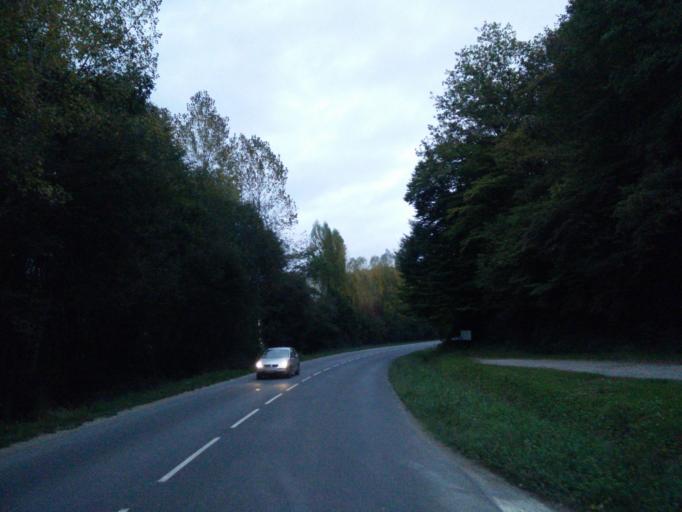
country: FR
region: Aquitaine
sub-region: Departement de la Dordogne
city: Carsac-Aillac
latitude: 44.8535
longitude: 1.2695
